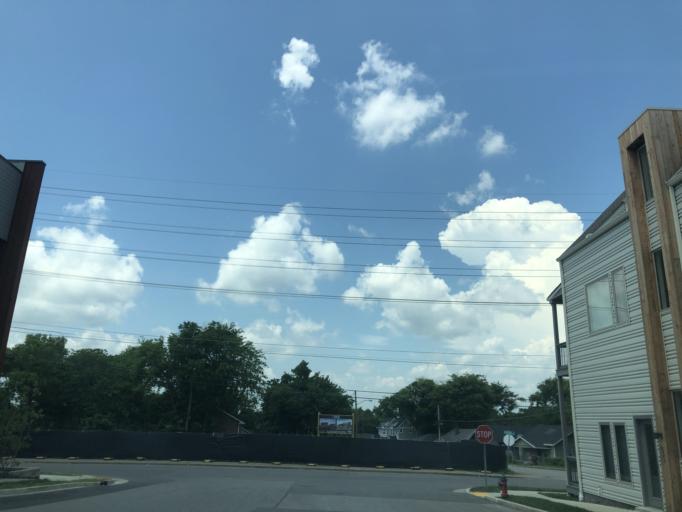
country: US
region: Tennessee
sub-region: Davidson County
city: Nashville
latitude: 36.1582
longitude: -86.8166
